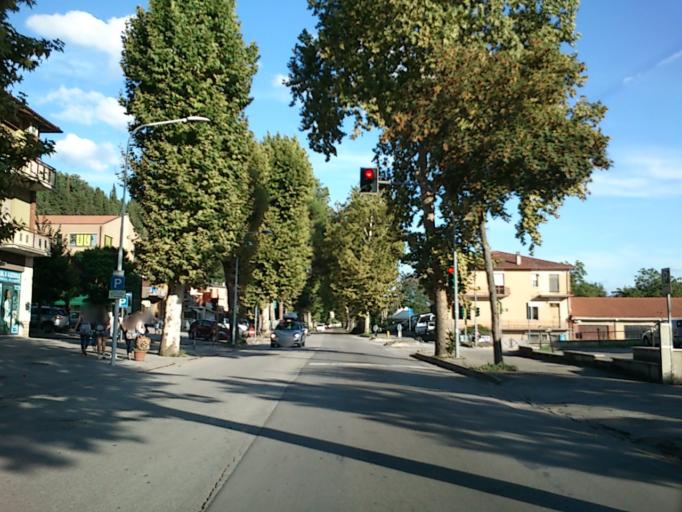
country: IT
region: The Marches
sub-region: Provincia di Pesaro e Urbino
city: Urbania
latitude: 43.6649
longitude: 12.5270
